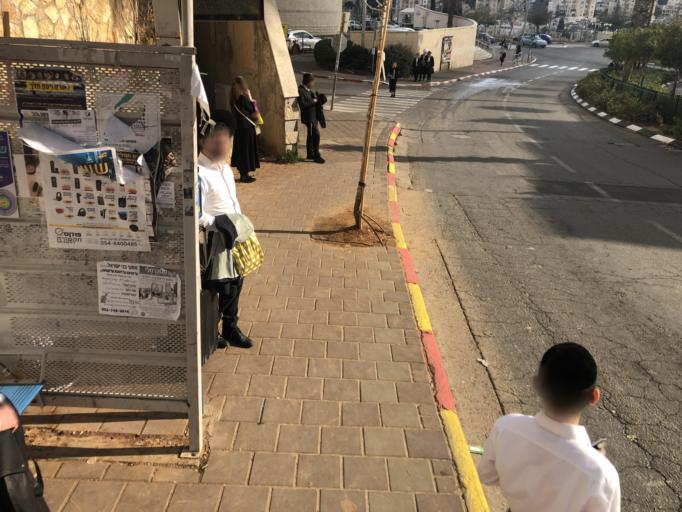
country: IL
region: Jerusalem
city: Modiin Ilit
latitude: 31.9371
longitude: 35.0381
